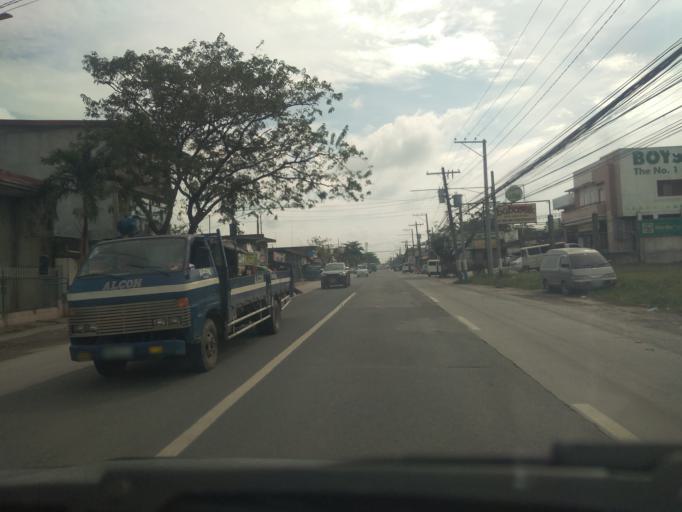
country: PH
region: Central Luzon
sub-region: Province of Pampanga
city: Pau
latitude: 15.0075
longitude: 120.7130
